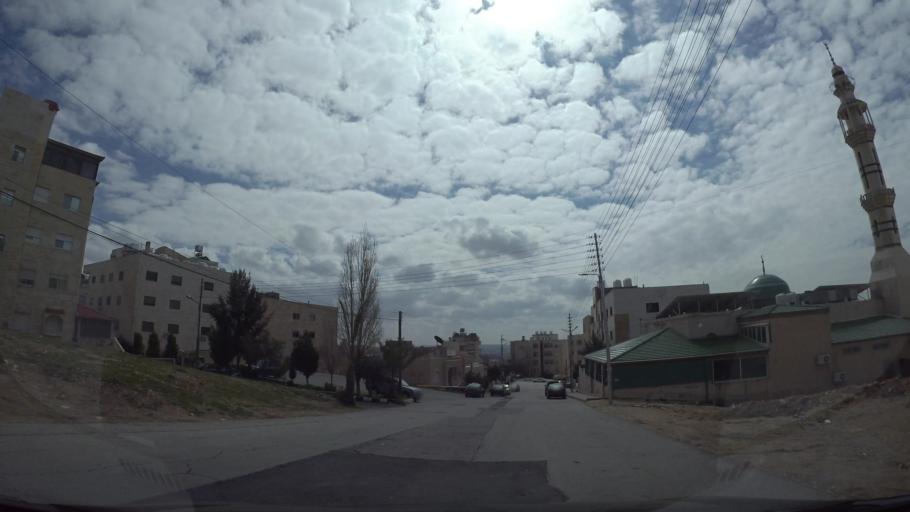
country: JO
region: Amman
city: Amman
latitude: 31.9972
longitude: 35.9133
